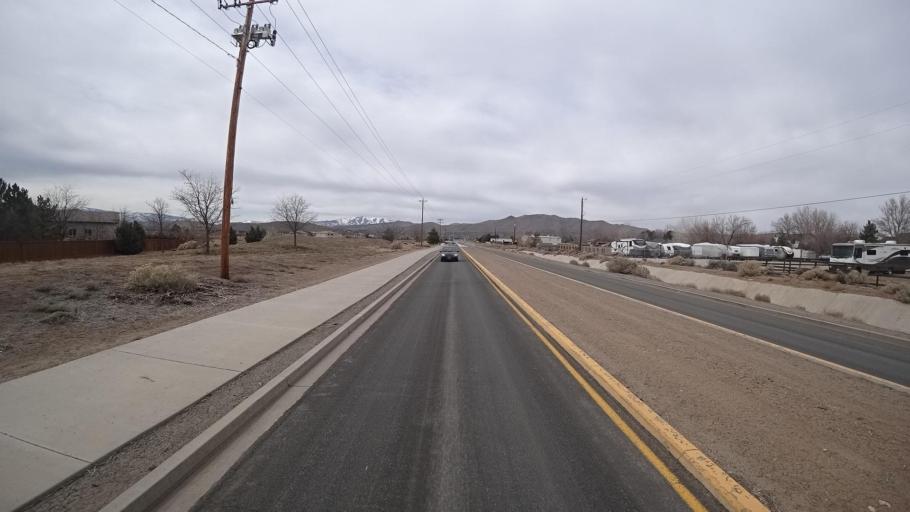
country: US
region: Nevada
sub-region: Washoe County
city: Spanish Springs
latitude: 39.6362
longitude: -119.6930
